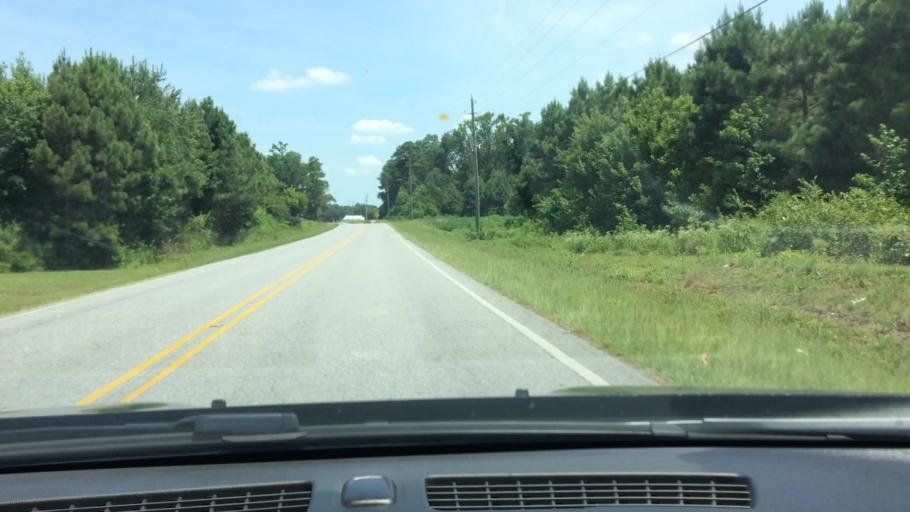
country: US
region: North Carolina
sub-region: Pitt County
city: Ayden
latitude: 35.4783
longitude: -77.3785
